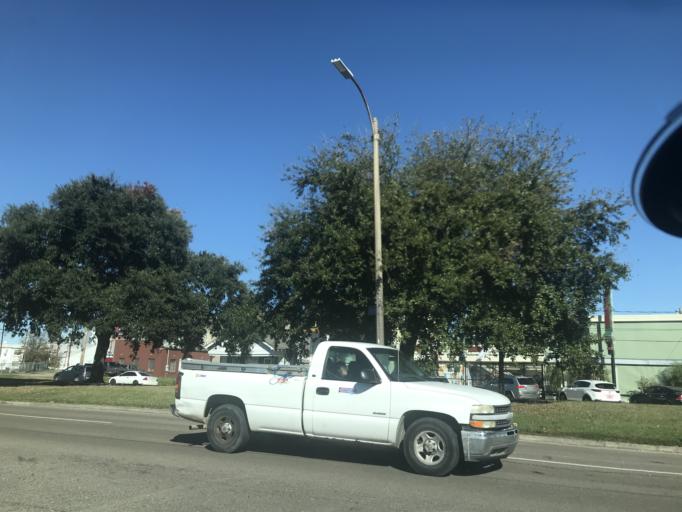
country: US
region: Louisiana
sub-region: Orleans Parish
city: New Orleans
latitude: 29.9513
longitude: -90.0975
